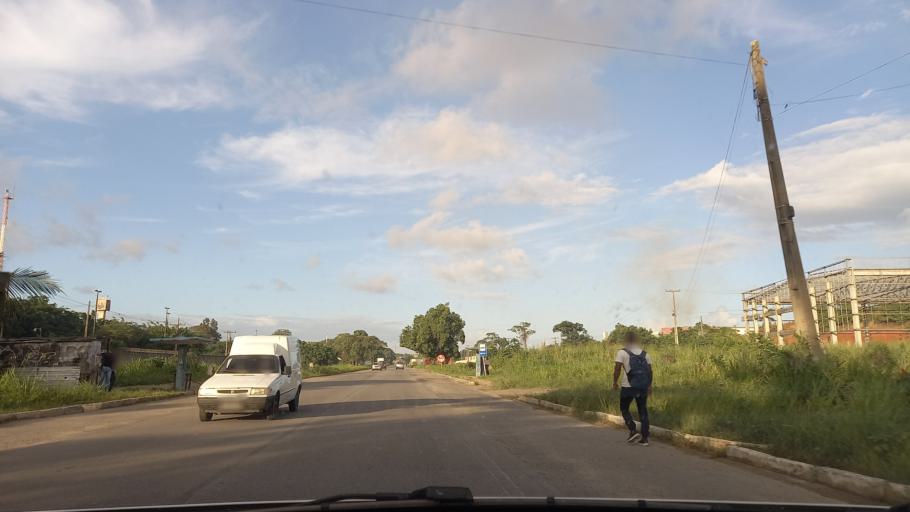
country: BR
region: Pernambuco
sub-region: Cabo De Santo Agostinho
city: Cabo
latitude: -8.2492
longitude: -35.0033
